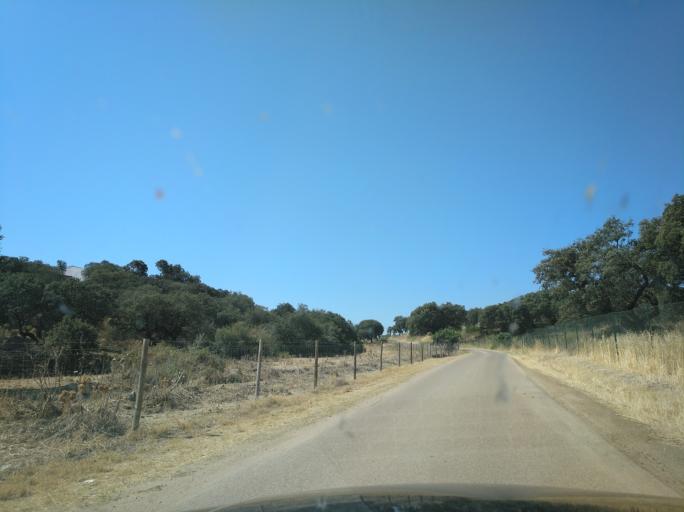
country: PT
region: Portalegre
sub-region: Campo Maior
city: Campo Maior
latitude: 39.0496
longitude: -6.9989
